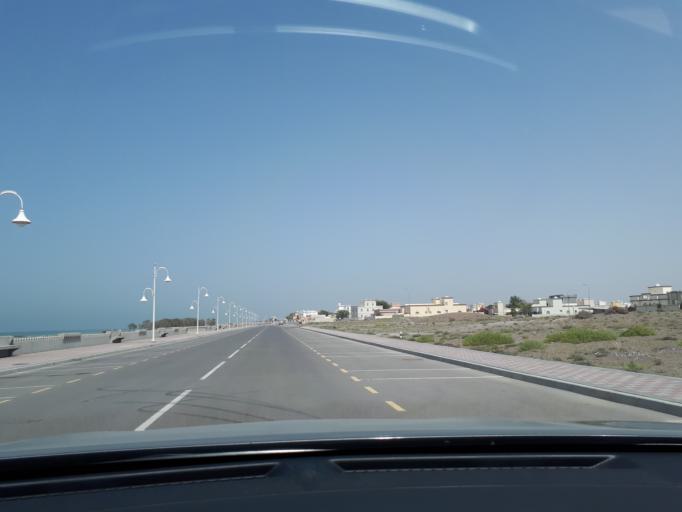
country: OM
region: Muhafazat Masqat
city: As Sib al Jadidah
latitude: 23.7123
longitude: 58.0679
